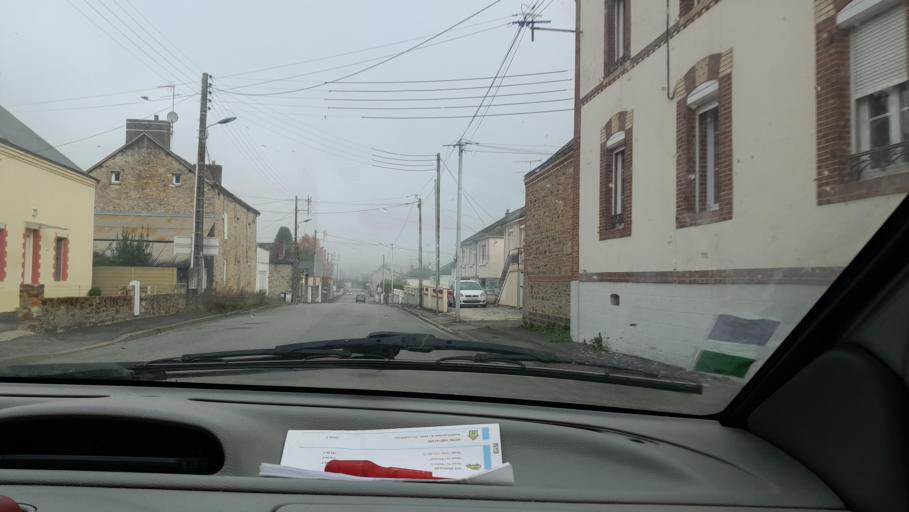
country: FR
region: Pays de la Loire
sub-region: Departement de la Mayenne
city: Saint-Pierre-la-Cour
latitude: 48.1099
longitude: -1.0241
